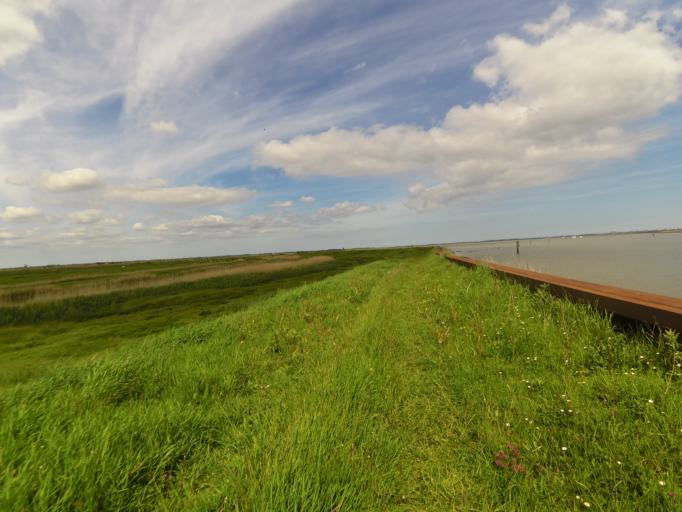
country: GB
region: England
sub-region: Norfolk
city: Great Yarmouth
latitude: 52.5966
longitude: 1.6513
